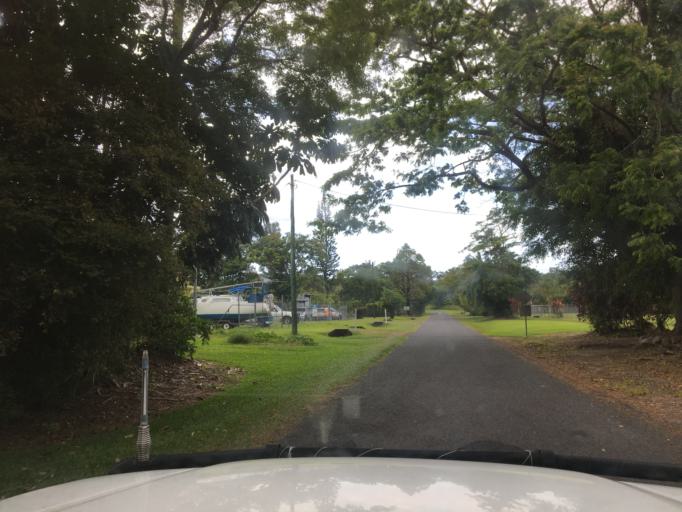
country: AU
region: Queensland
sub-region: Cairns
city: Woree
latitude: -17.2186
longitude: 145.9148
